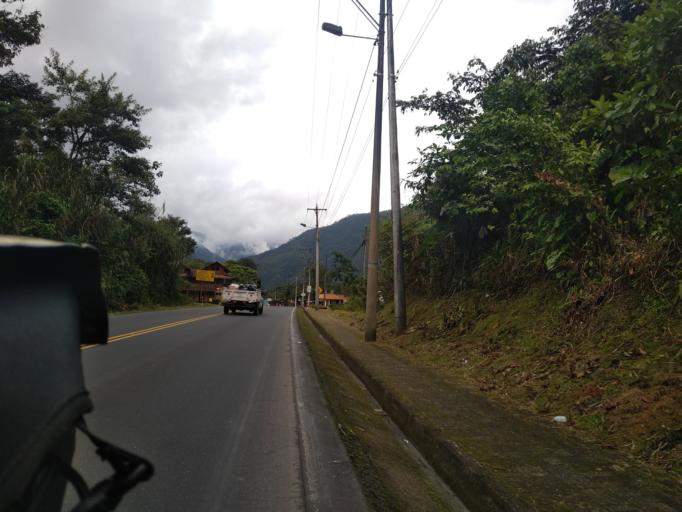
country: EC
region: Tungurahua
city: Banos
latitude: -1.4139
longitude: -78.2180
